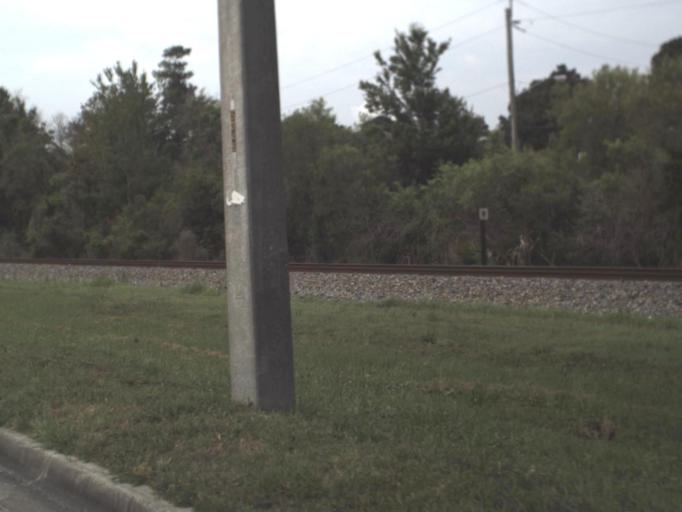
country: US
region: Florida
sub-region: Clay County
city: Bellair-Meadowbrook Terrace
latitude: 30.2524
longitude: -81.6990
